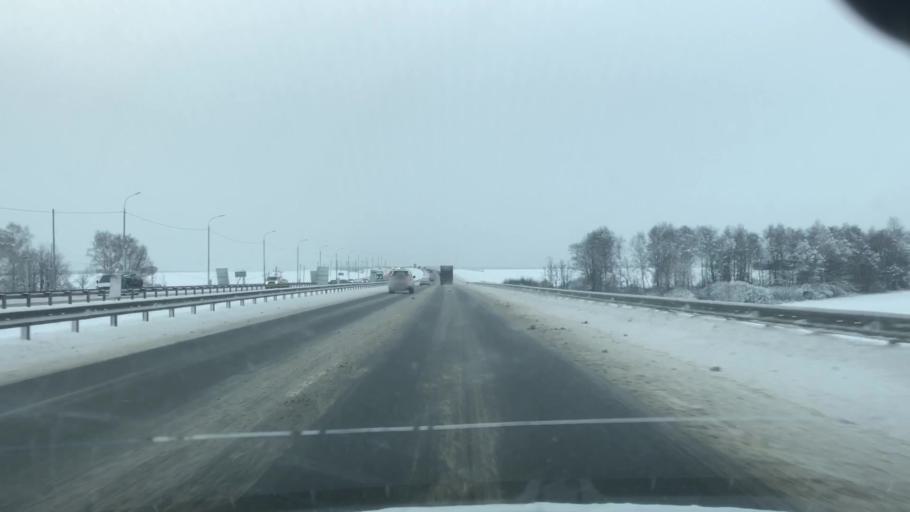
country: RU
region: Moskovskaya
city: Mikhnevo
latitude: 55.1134
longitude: 37.9262
